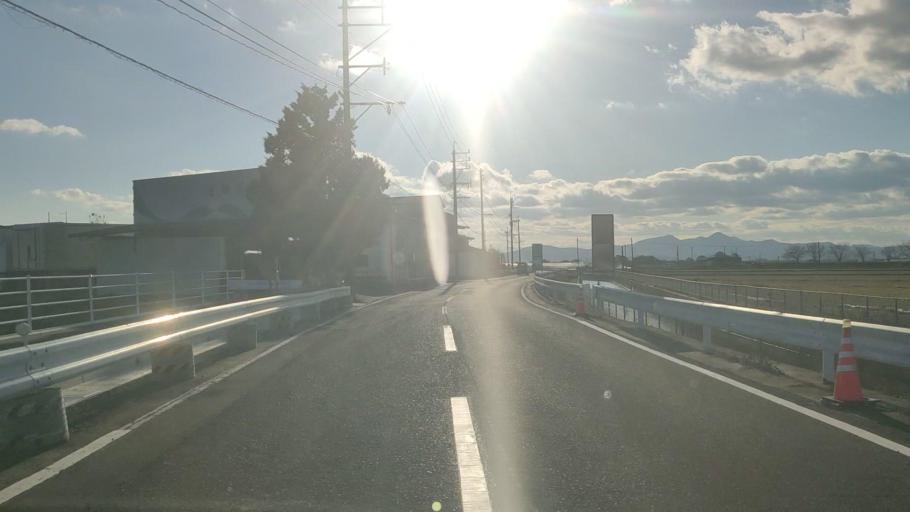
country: JP
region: Saga Prefecture
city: Saga-shi
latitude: 33.3024
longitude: 130.2536
